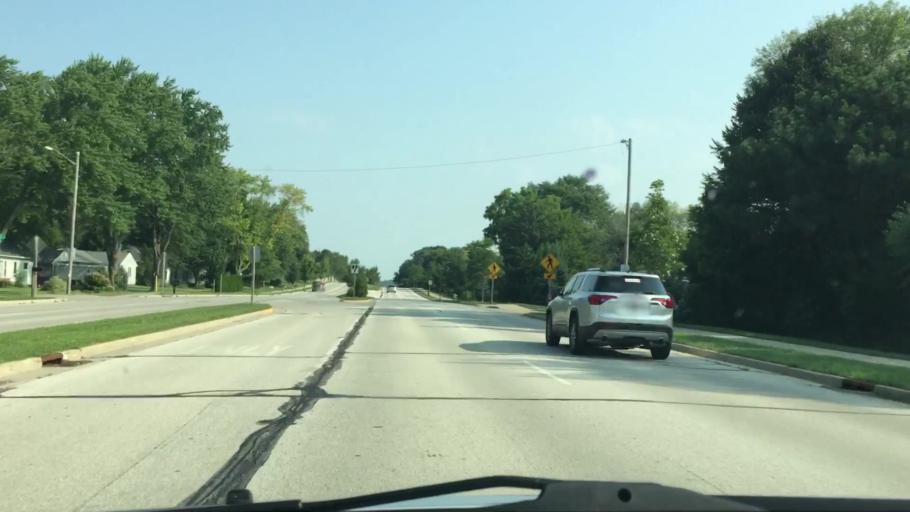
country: US
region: Wisconsin
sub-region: Waukesha County
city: Brookfield
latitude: 43.0200
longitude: -88.1269
